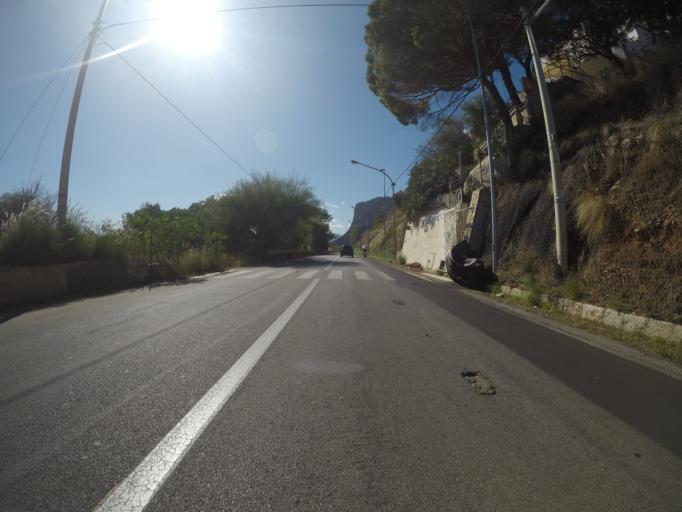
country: IT
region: Sicily
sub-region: Palermo
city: Palermo
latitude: 38.1766
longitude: 13.3660
